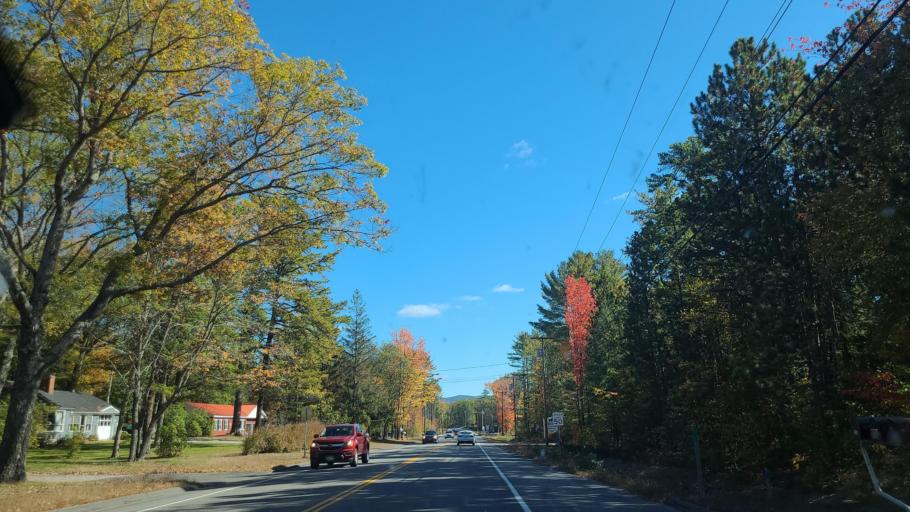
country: US
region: Maine
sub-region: Oxford County
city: Fryeburg
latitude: 44.0210
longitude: -70.9571
